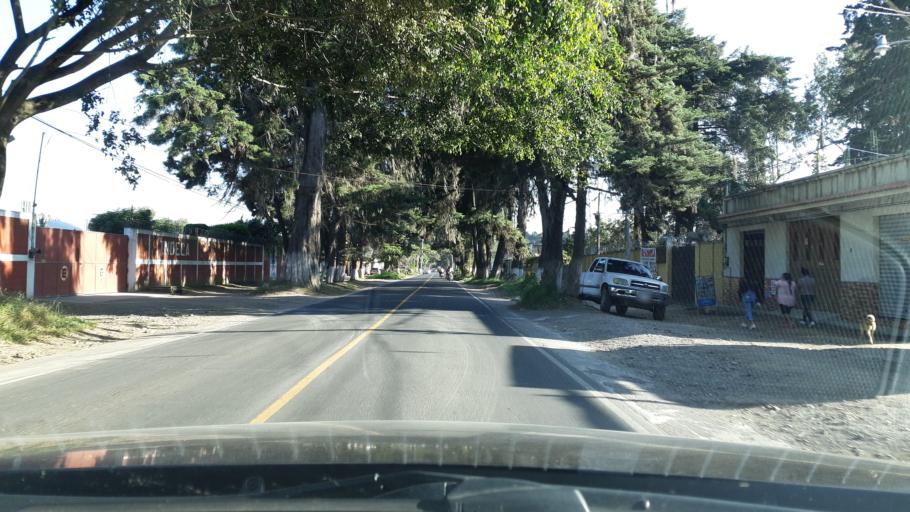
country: GT
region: Chimaltenango
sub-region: Municipio de Chimaltenango
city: Chimaltenango
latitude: 14.6458
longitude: -90.8117
